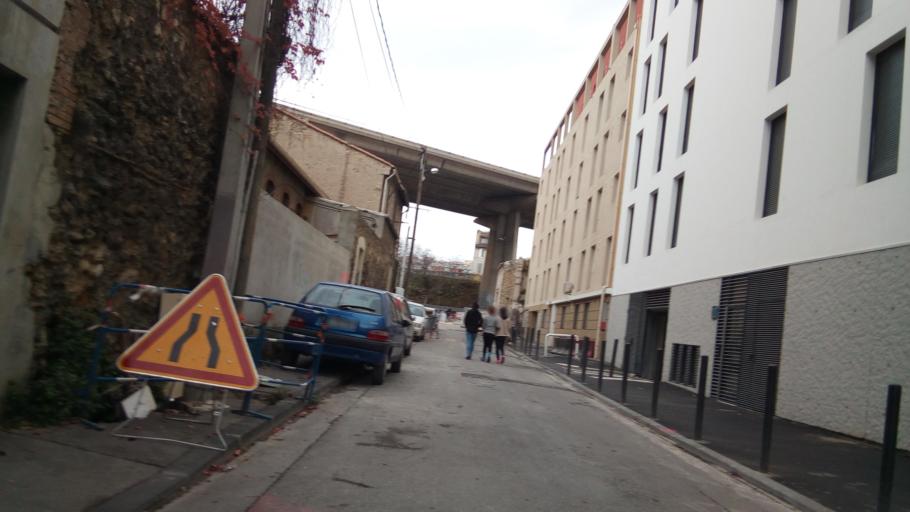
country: FR
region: Provence-Alpes-Cote d'Azur
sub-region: Departement des Bouches-du-Rhone
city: Marseille 03
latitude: 43.3144
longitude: 5.3739
